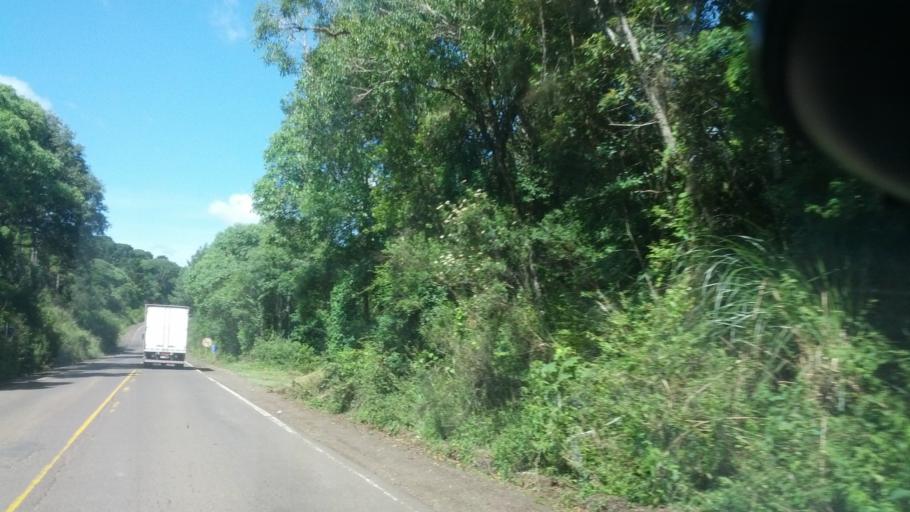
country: BR
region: Santa Catarina
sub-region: Lages
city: Lages
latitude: -27.9252
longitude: -50.5466
